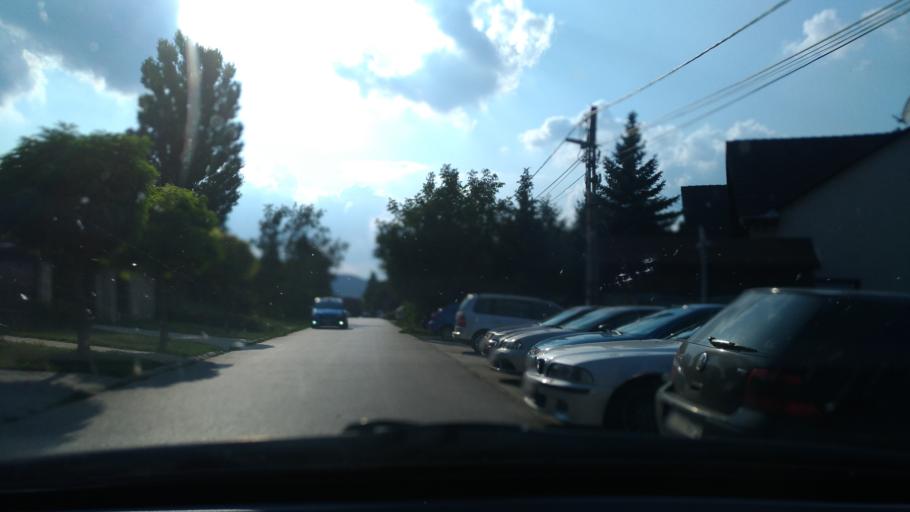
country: HU
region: Pest
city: Solymar
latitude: 47.5963
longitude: 18.9432
